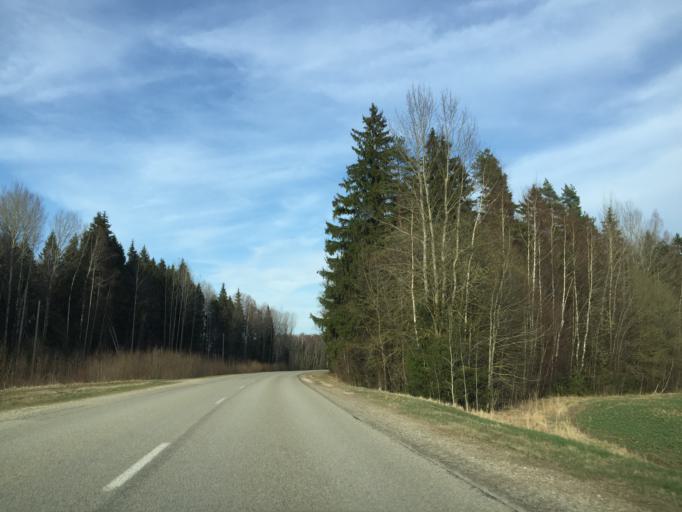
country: LV
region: Lielvarde
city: Lielvarde
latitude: 56.7916
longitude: 24.8085
